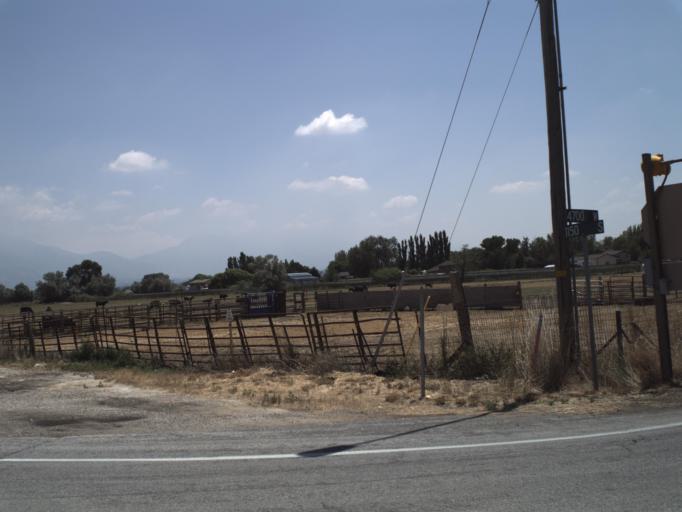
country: US
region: Utah
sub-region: Weber County
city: Plain City
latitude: 41.2459
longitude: -112.0955
